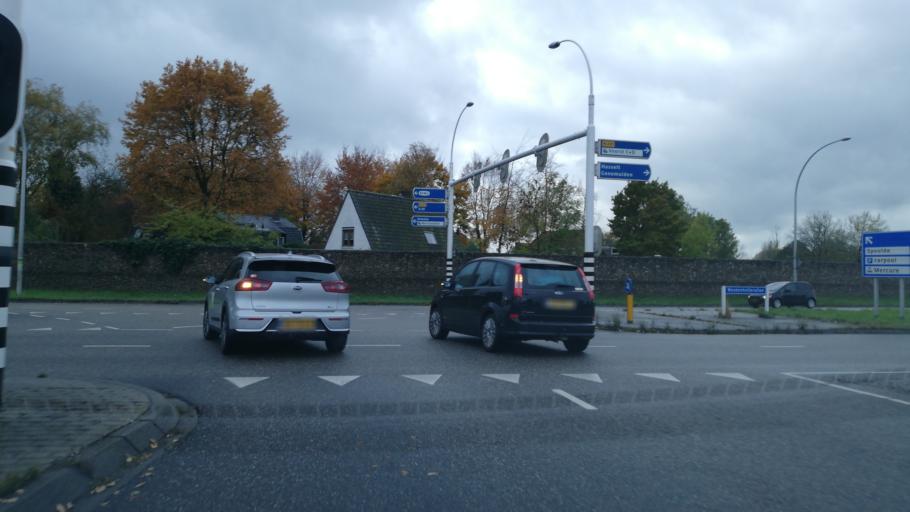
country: NL
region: Overijssel
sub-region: Gemeente Zwolle
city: Zwolle
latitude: 52.5094
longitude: 6.0627
